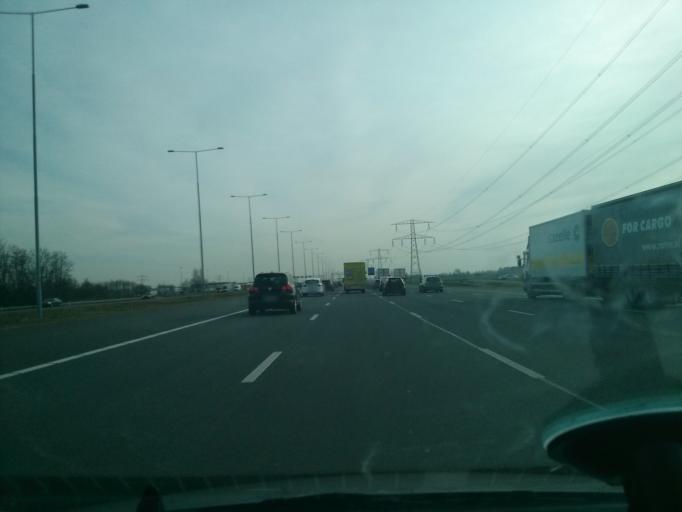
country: NL
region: Utrecht
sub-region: Stichtse Vecht
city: Breukelen
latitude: 52.1897
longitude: 4.9863
